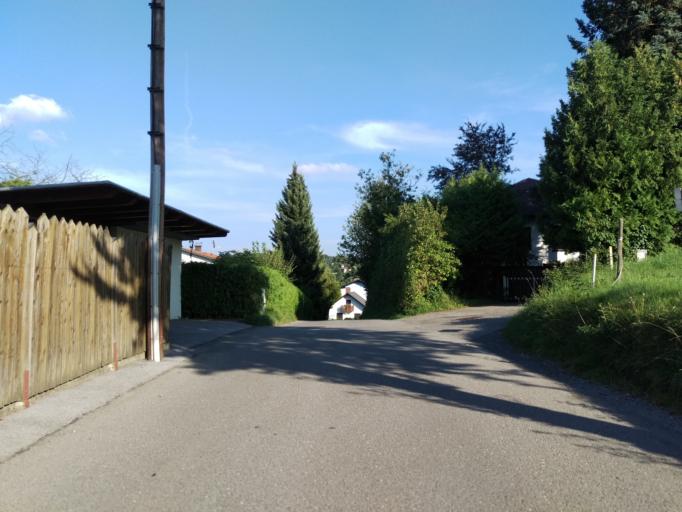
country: AT
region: Styria
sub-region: Graz Stadt
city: Mariatrost
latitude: 47.0718
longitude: 15.4967
